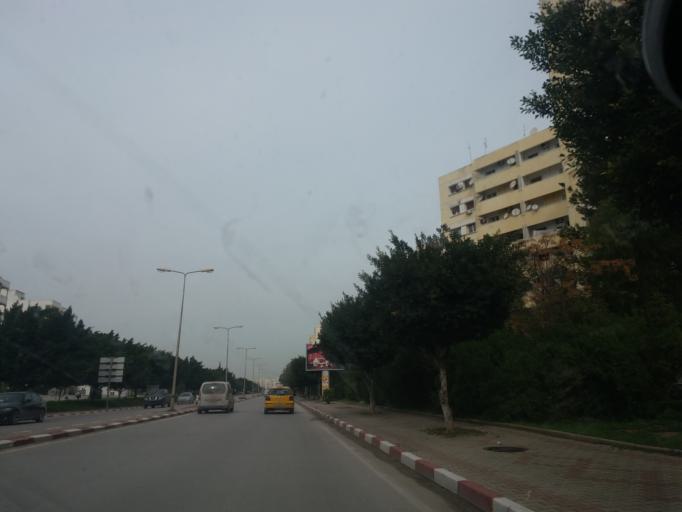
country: TN
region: Tunis
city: Tunis
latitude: 36.8445
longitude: 10.1637
